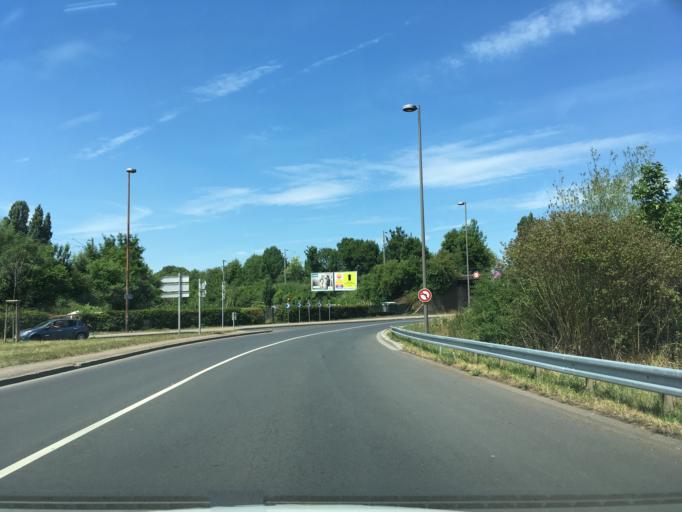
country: FR
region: Lorraine
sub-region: Departement de la Moselle
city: Metz
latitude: 49.1355
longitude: 6.1732
